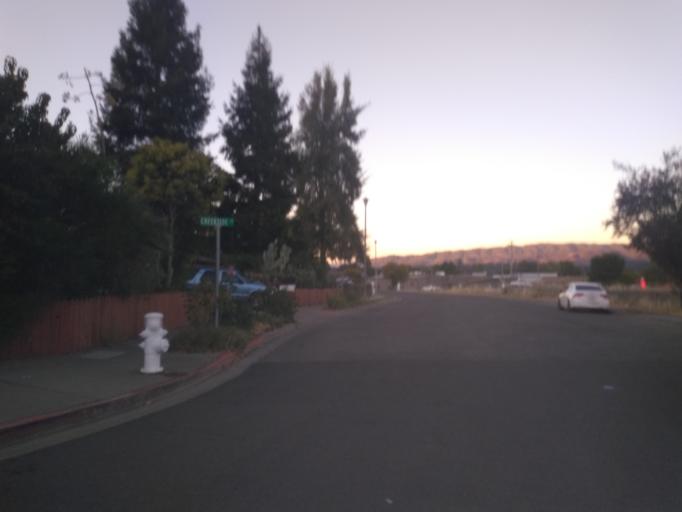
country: US
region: California
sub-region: Mendocino County
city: Ukiah
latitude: 39.1353
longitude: -123.2068
